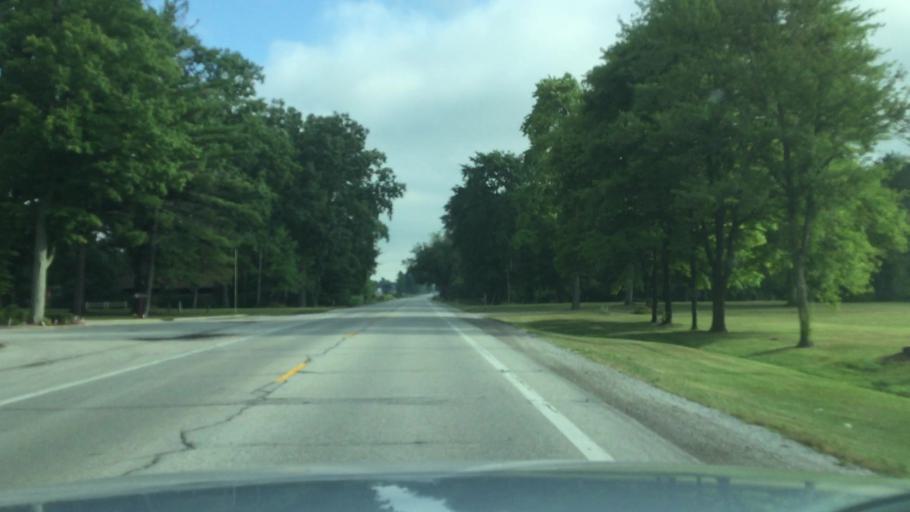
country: US
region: Michigan
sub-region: Saginaw County
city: Birch Run
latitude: 43.2541
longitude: -83.7355
